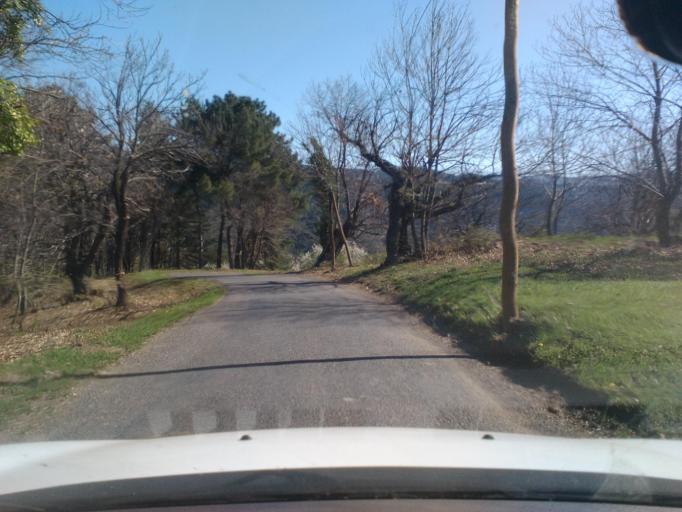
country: FR
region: Languedoc-Roussillon
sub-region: Departement du Gard
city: Saint-Jean-du-Gard
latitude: 44.1579
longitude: 3.7670
